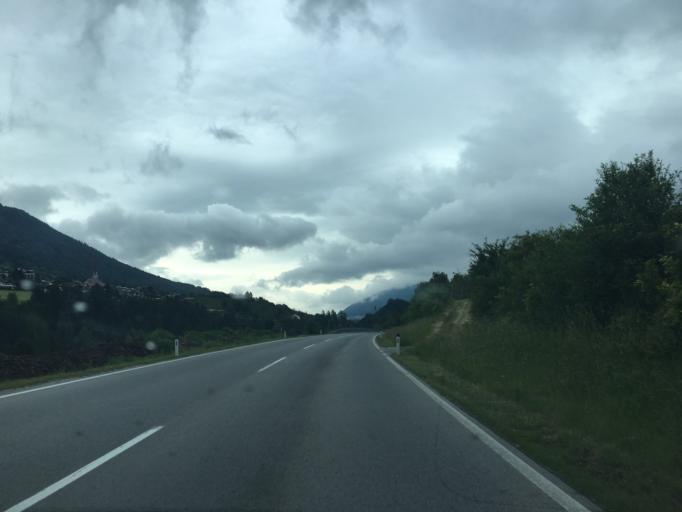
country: AT
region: Tyrol
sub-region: Politischer Bezirk Innsbruck Land
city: Telfes im Stubai
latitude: 47.1567
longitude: 11.3593
